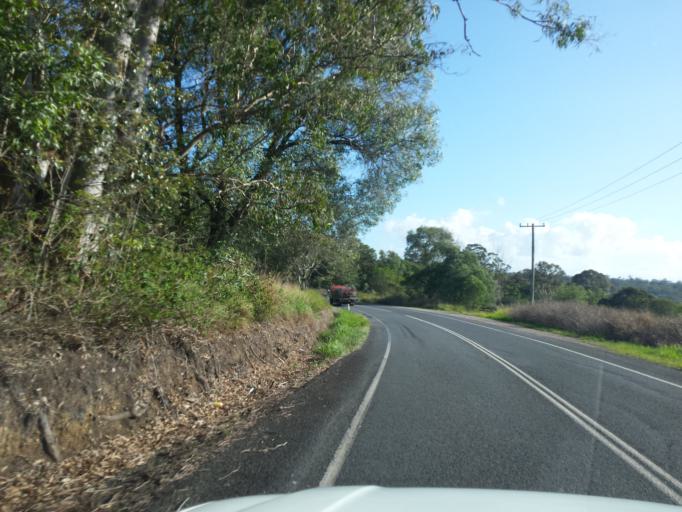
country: AU
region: Queensland
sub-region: Logan
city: Windaroo
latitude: -27.7710
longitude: 153.1904
